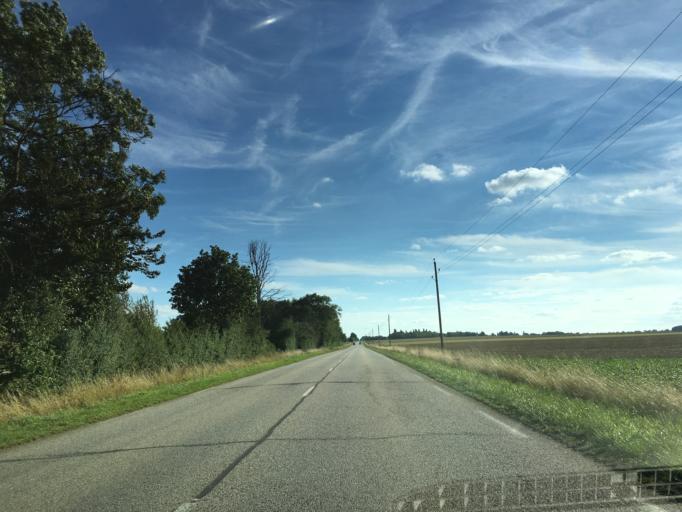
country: FR
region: Lower Normandy
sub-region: Departement du Calvados
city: Orbec
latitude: 48.9288
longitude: 0.4381
